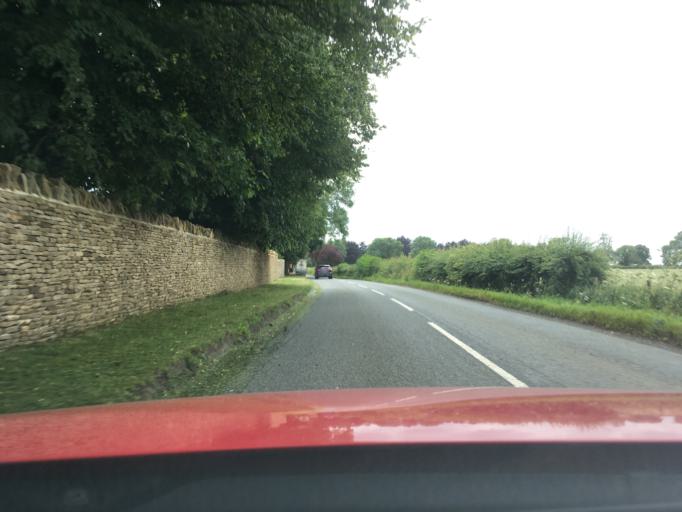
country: GB
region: England
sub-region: Gloucestershire
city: Chipping Campden
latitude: 52.0540
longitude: -1.7981
